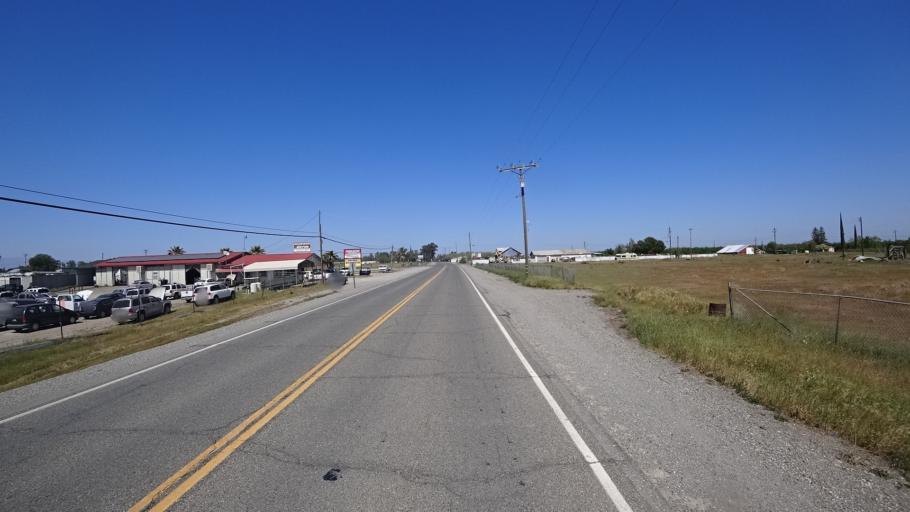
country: US
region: California
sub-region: Glenn County
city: Orland
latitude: 39.6957
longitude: -122.1965
